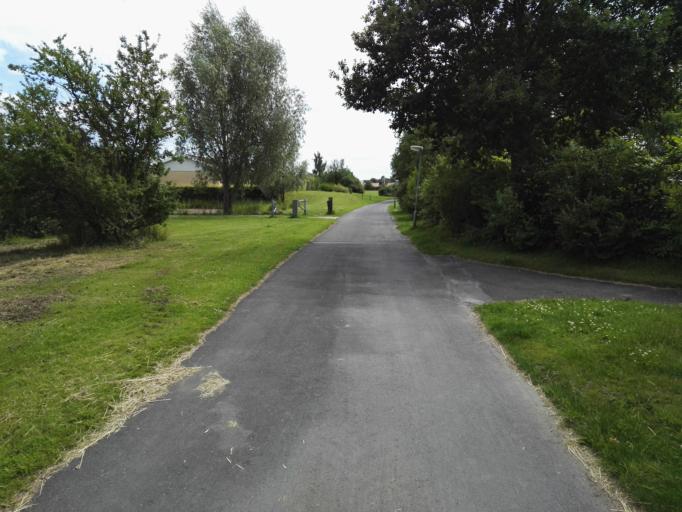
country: DK
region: Capital Region
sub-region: Ballerup Kommune
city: Malov
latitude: 55.7540
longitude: 12.3298
